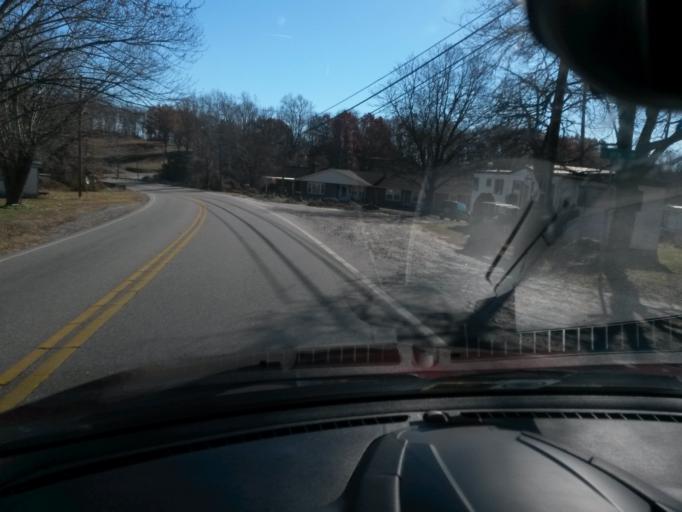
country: US
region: Virginia
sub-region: Henry County
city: Bassett
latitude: 36.7611
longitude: -80.0221
